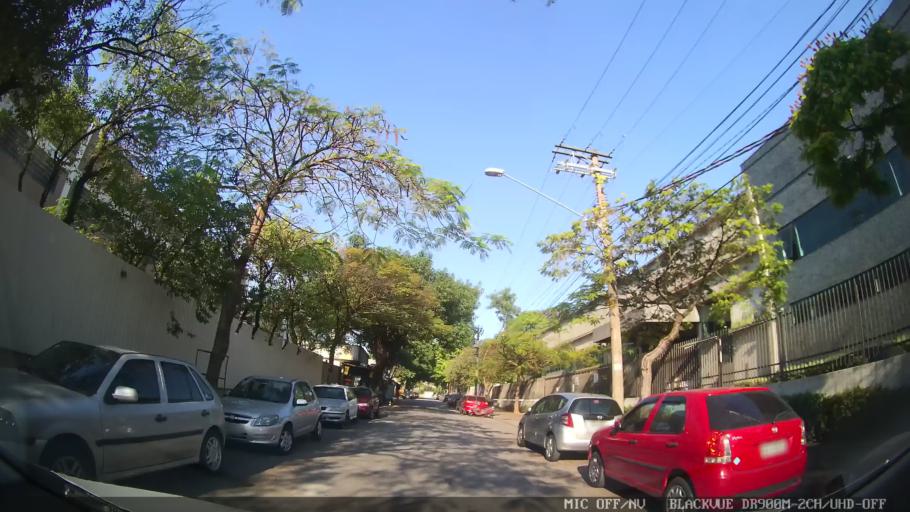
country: BR
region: Sao Paulo
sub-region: Sao Paulo
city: Sao Paulo
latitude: -23.5098
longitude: -46.6692
